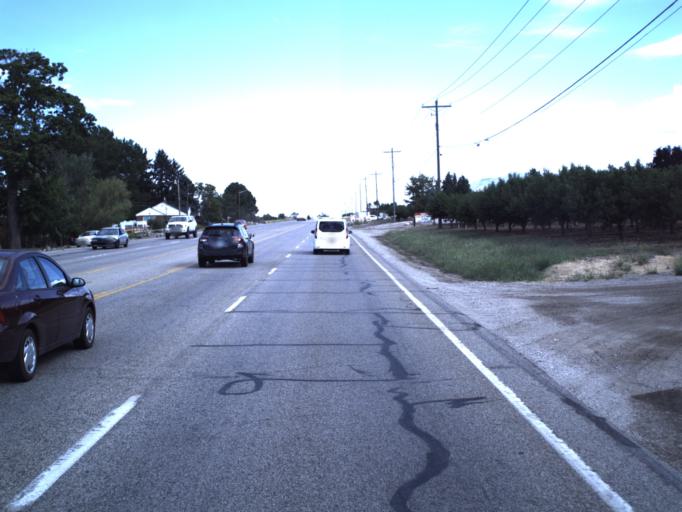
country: US
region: Utah
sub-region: Box Elder County
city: Perry
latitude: 41.4453
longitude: -112.0373
